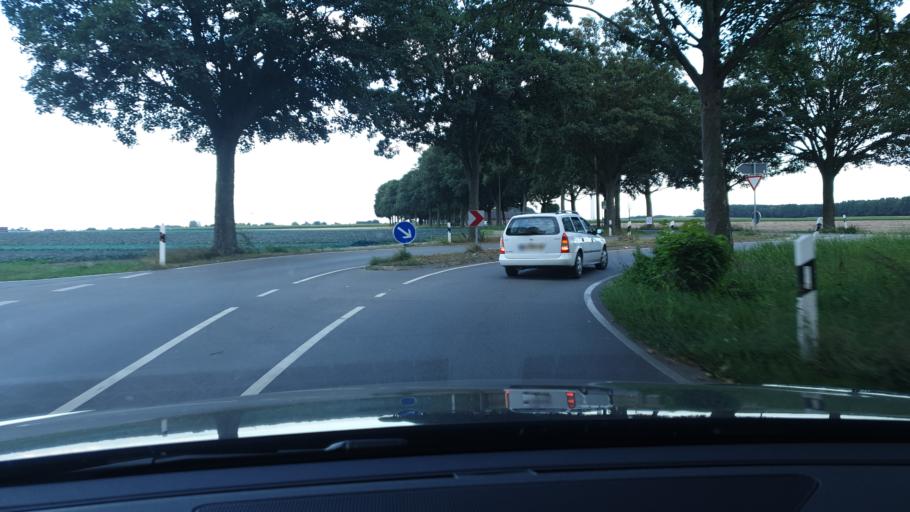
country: NL
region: Limburg
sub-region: Gemeente Venlo
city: Arcen
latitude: 51.4737
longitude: 6.2250
